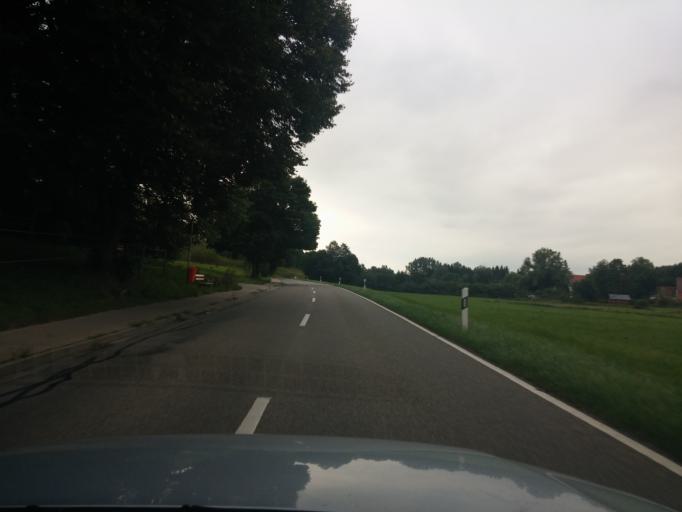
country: DE
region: Bavaria
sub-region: Swabia
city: Buxheim
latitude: 47.9789
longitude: 10.1491
